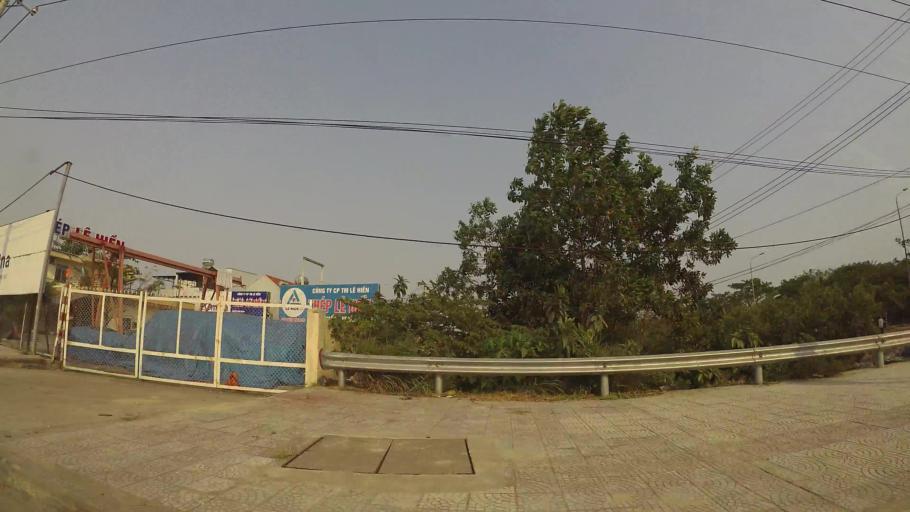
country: VN
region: Da Nang
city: Cam Le
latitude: 16.0157
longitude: 108.1932
